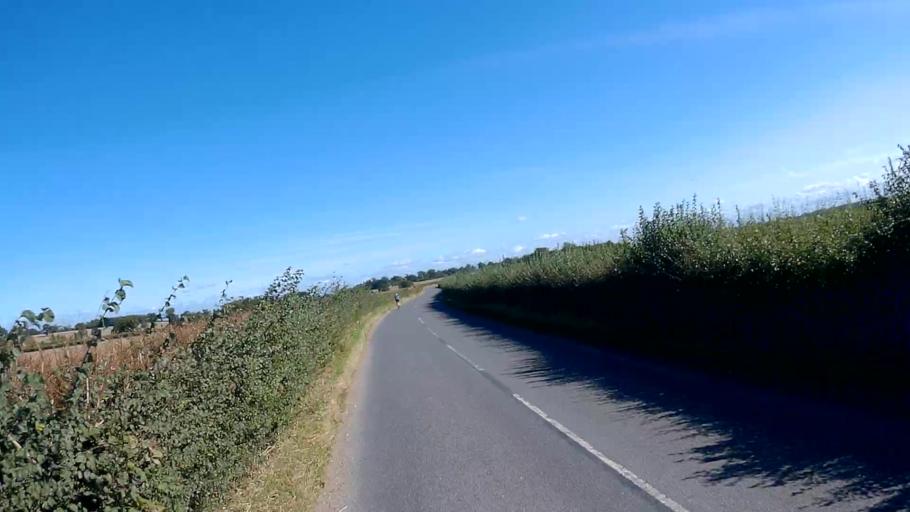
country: GB
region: England
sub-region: West Berkshire
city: Stratfield Mortimer
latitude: 51.3679
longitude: -1.0171
